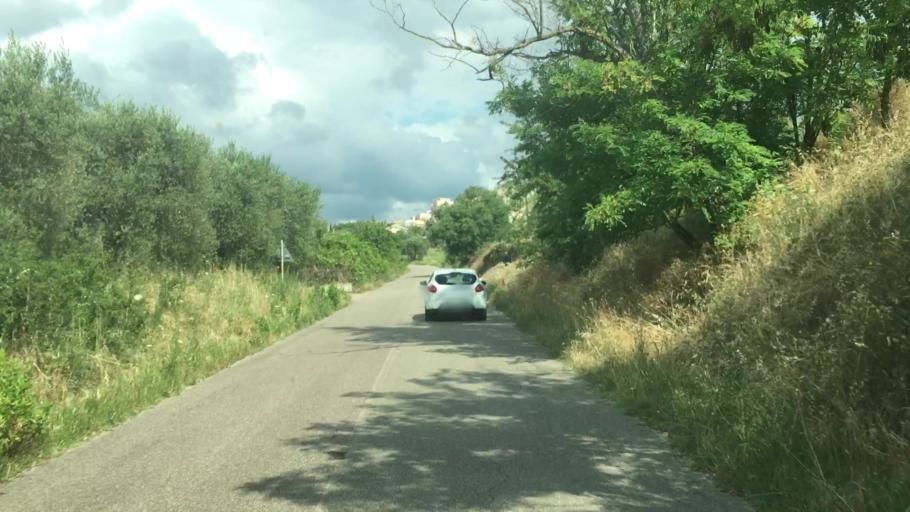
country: IT
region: Basilicate
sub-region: Provincia di Matera
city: San Mauro Forte
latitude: 40.4805
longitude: 16.2626
